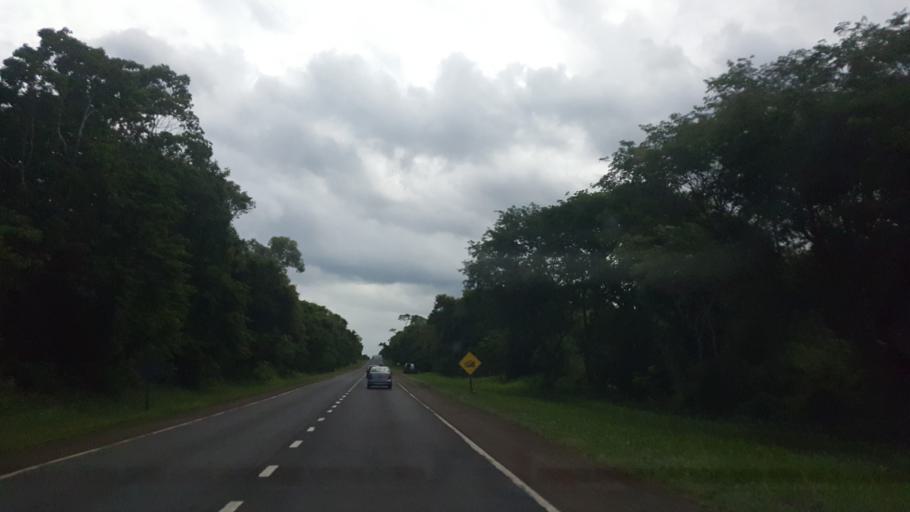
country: AR
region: Misiones
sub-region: Departamento de Iguazu
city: Puerto Iguazu
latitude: -25.7233
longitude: -54.5257
